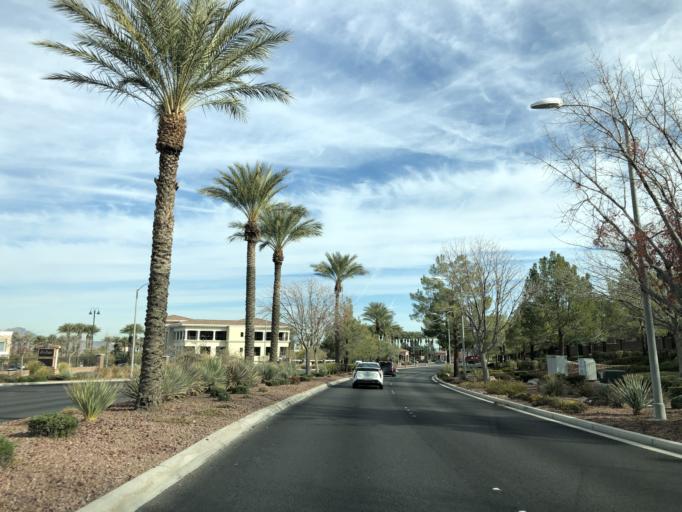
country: US
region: Nevada
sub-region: Clark County
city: Whitney
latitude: 36.0195
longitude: -115.0863
